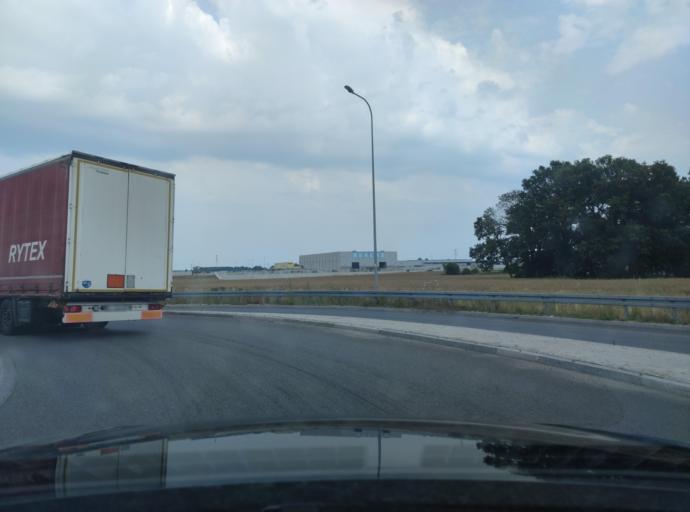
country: PL
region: Opole Voivodeship
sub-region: Powiat strzelecki
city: Strzelce Opolskie
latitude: 50.4632
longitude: 18.2753
